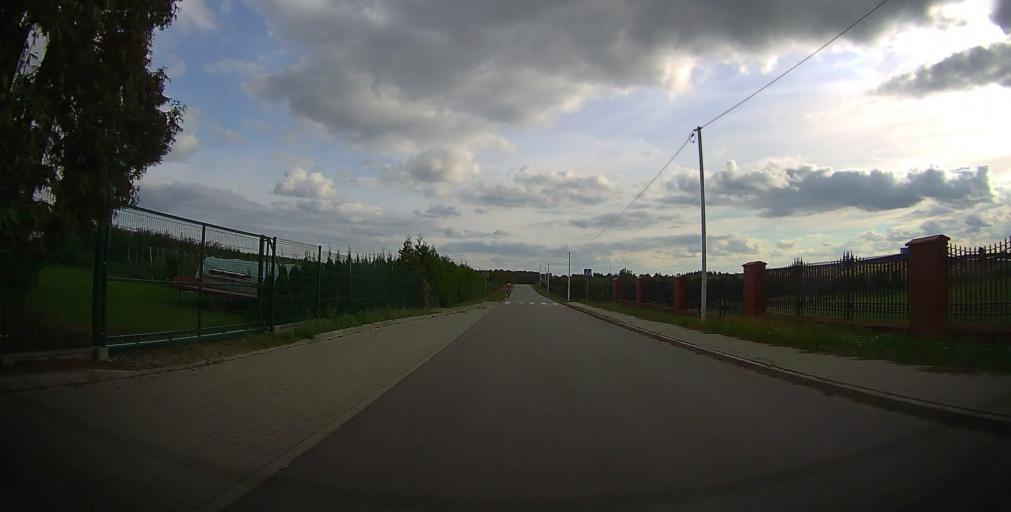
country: PL
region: Masovian Voivodeship
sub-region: Powiat bialobrzeski
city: Promna
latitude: 51.7112
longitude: 20.9582
